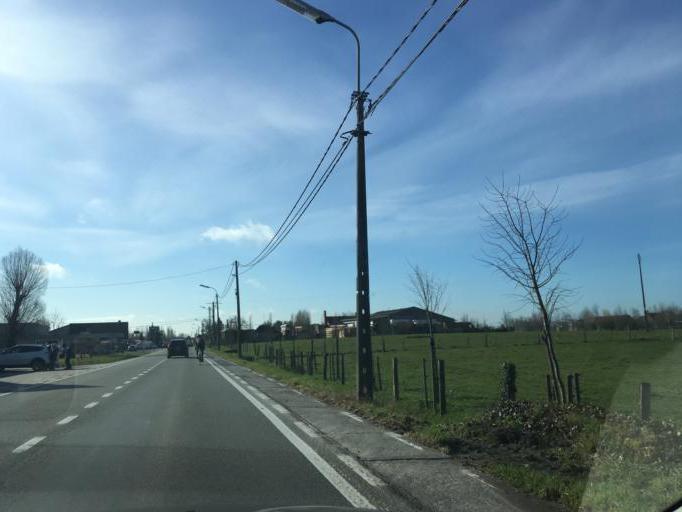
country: BE
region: Flanders
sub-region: Provincie West-Vlaanderen
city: Ledegem
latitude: 50.8645
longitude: 3.1518
